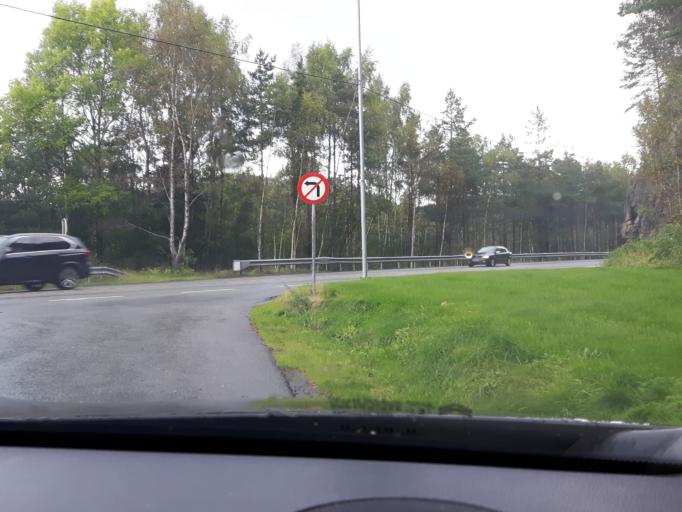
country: NO
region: Vest-Agder
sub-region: Marnardal
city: Helland
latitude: 58.0872
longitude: 7.6210
